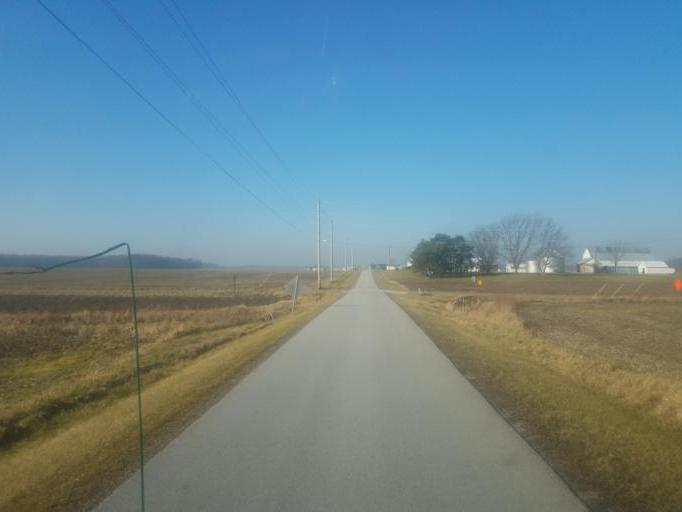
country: US
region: Ohio
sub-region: Crawford County
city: Bucyrus
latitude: 41.0082
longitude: -82.9387
